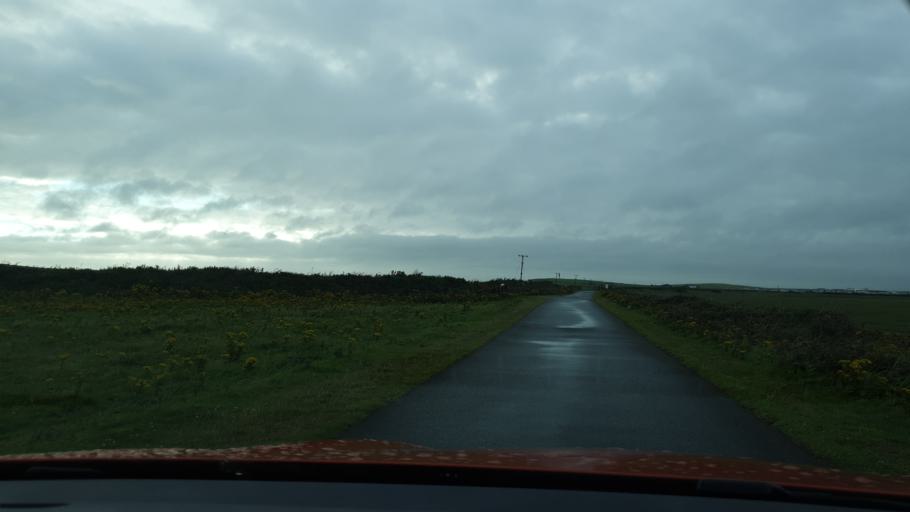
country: GB
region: England
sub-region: Cumbria
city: Barrow in Furness
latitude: 54.0501
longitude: -3.2018
